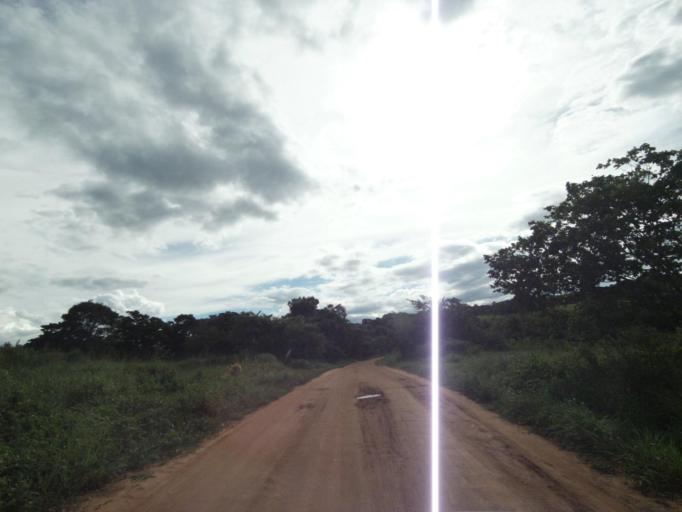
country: BR
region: Goias
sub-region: Jaragua
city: Jaragua
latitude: -15.8428
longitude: -49.3594
